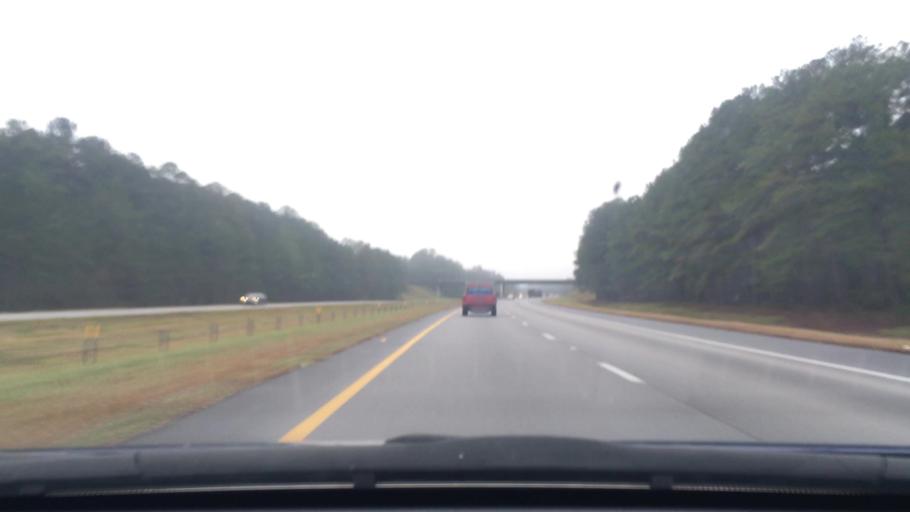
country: US
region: South Carolina
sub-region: Lee County
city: Bishopville
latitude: 34.1964
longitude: -80.3355
